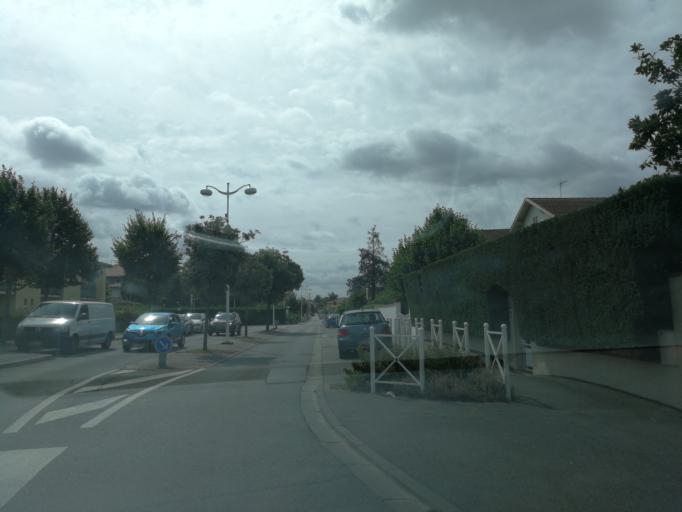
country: FR
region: Midi-Pyrenees
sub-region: Departement de la Haute-Garonne
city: Balma
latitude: 43.6144
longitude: 1.4936
